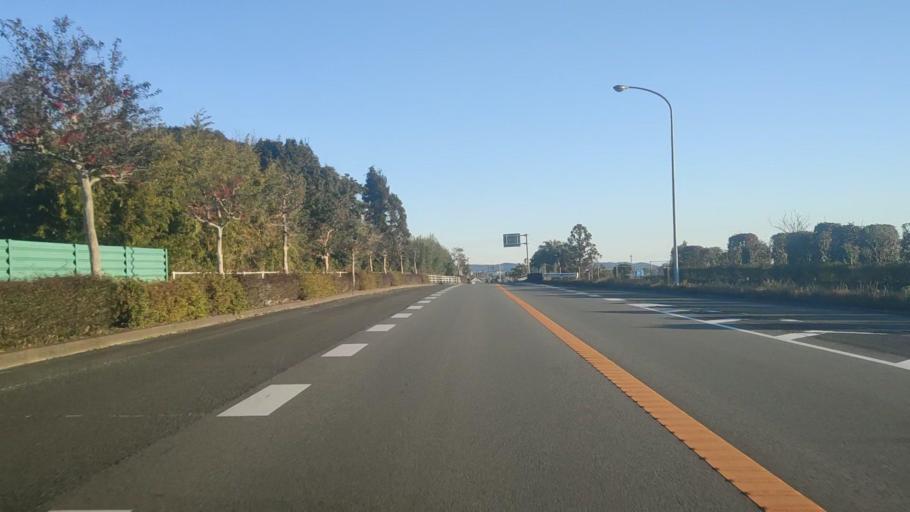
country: JP
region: Miyazaki
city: Tsuma
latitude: 32.0379
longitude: 131.4672
